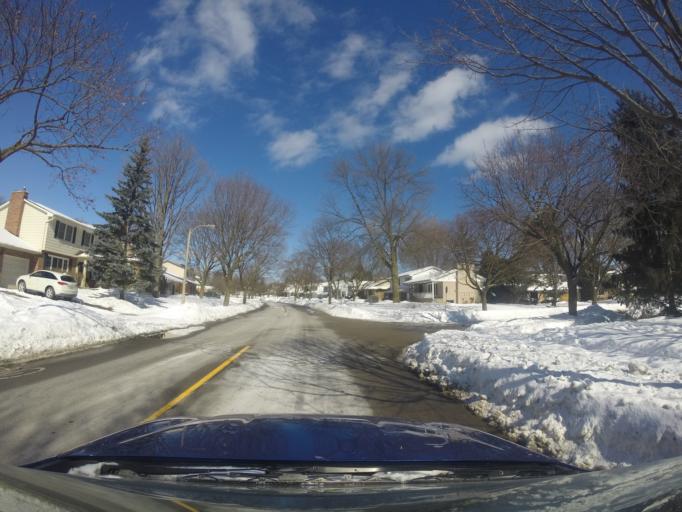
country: CA
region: Ontario
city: Burlington
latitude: 43.3466
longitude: -79.7677
